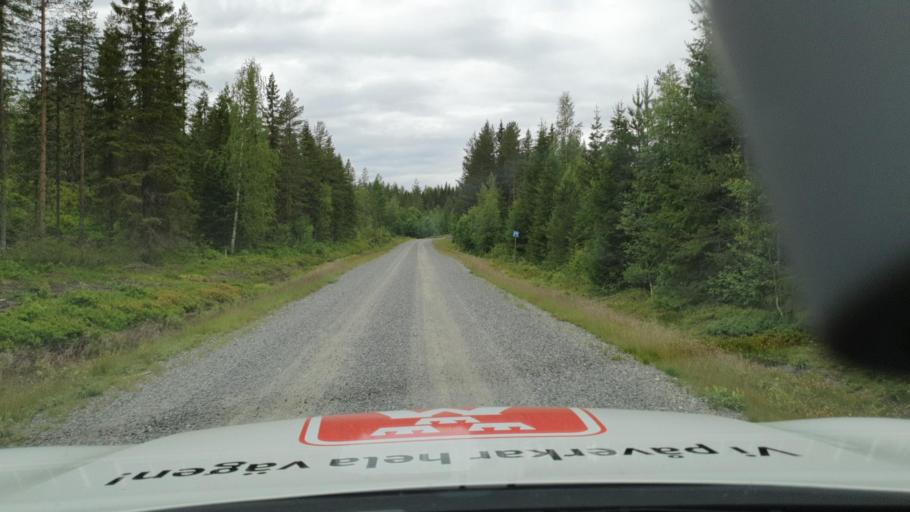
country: SE
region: Vaesterbotten
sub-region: Nordmalings Kommun
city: Nordmaling
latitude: 63.7384
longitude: 19.3991
